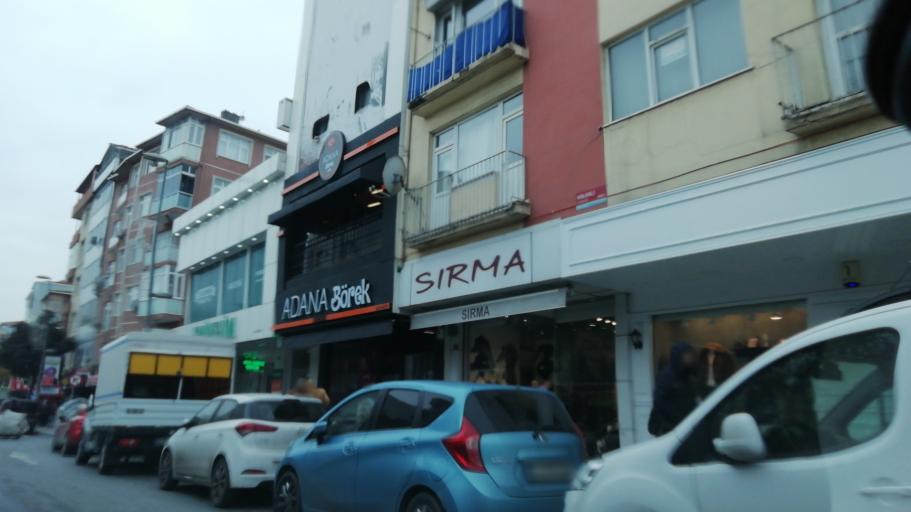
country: TR
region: Istanbul
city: Mahmutbey
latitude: 41.0027
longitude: 28.7979
